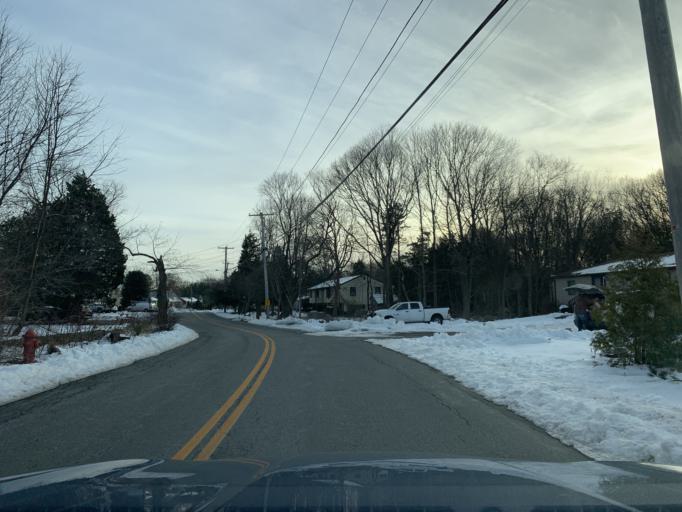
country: US
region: Rhode Island
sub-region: Washington County
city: North Kingstown
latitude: 41.5876
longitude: -71.4349
